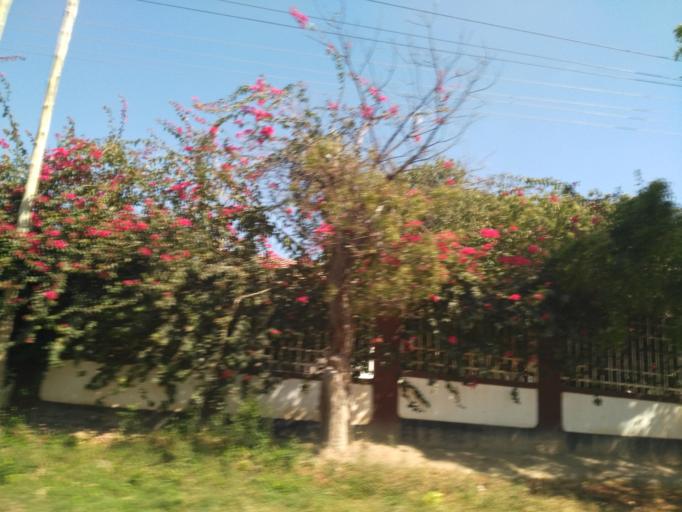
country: TZ
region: Dodoma
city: Dodoma
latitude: -6.1620
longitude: 35.7615
